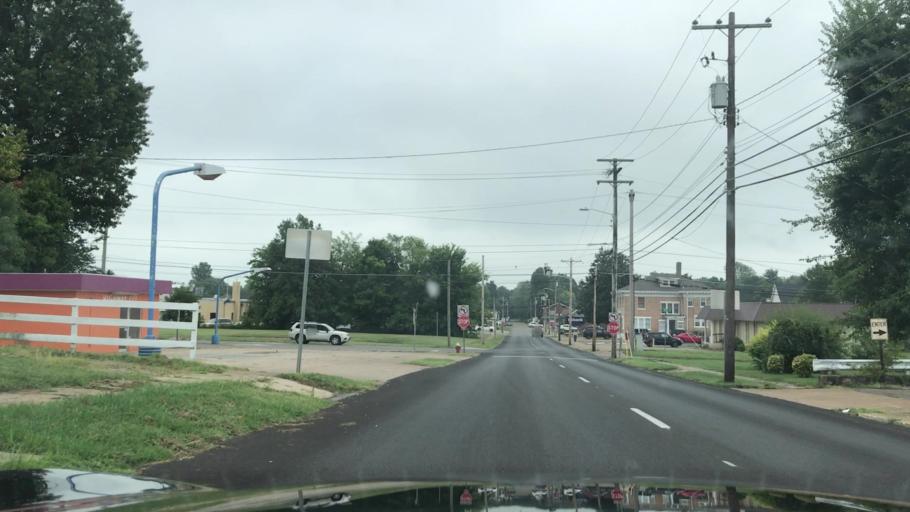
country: US
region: Kentucky
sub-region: Graves County
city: Mayfield
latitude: 36.7383
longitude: -88.6378
